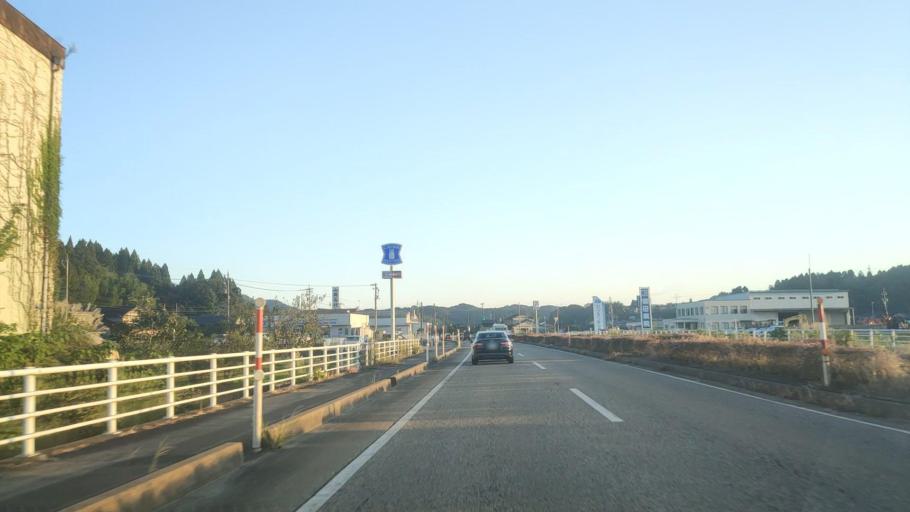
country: JP
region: Toyama
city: Himi
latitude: 36.8200
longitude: 136.9949
